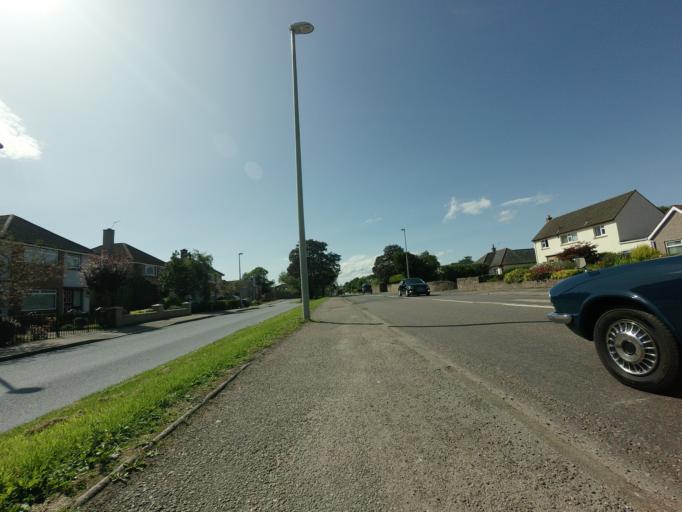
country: GB
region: Scotland
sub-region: Highland
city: Inverness
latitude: 57.4726
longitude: -4.1952
